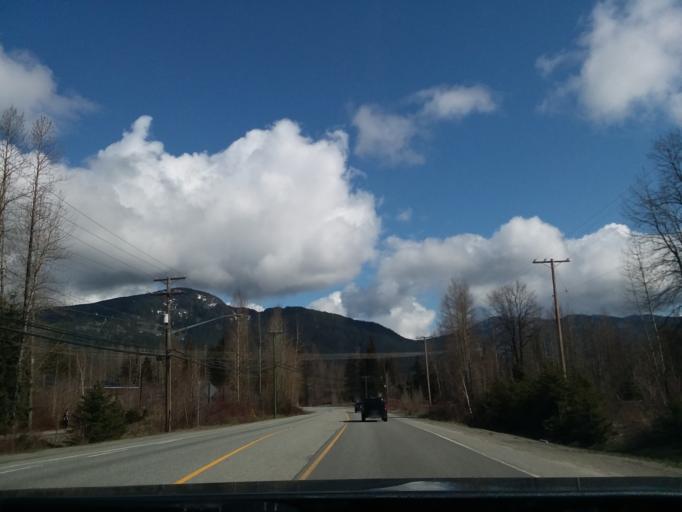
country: CA
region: British Columbia
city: Whistler
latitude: 50.1336
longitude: -122.9533
